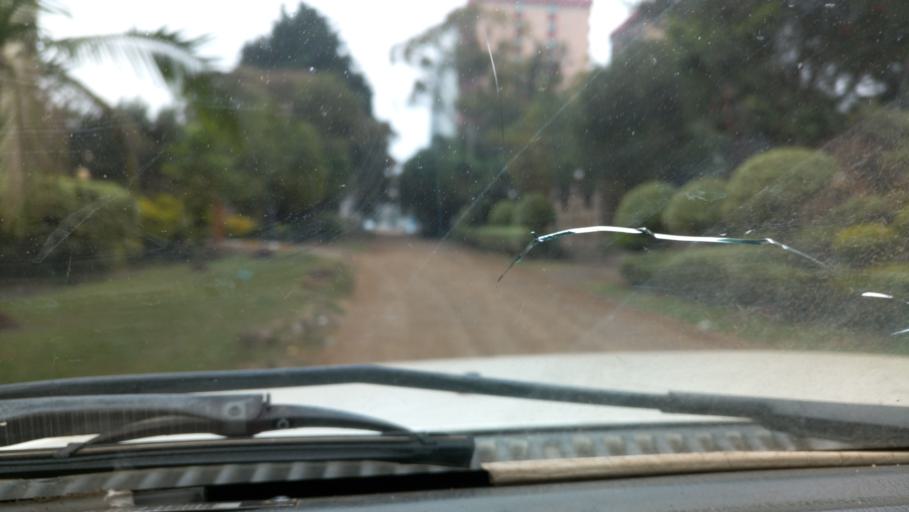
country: KE
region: Nairobi Area
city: Nairobi
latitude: -1.2862
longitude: 36.7887
